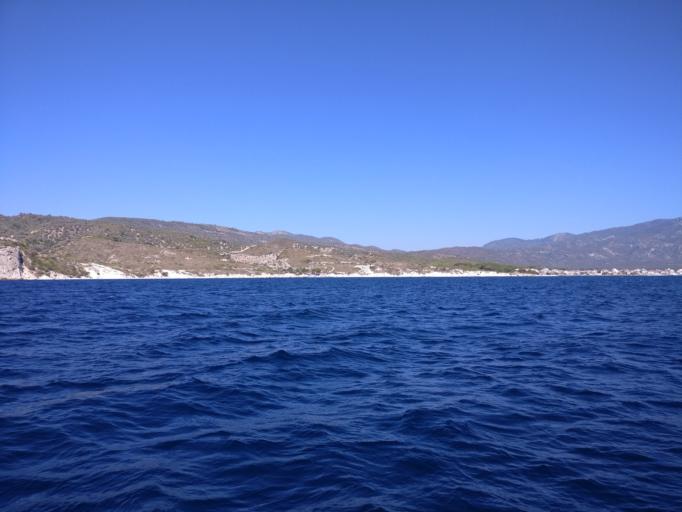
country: GR
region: North Aegean
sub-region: Nomos Samou
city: Chora
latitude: 37.6503
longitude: 26.8919
